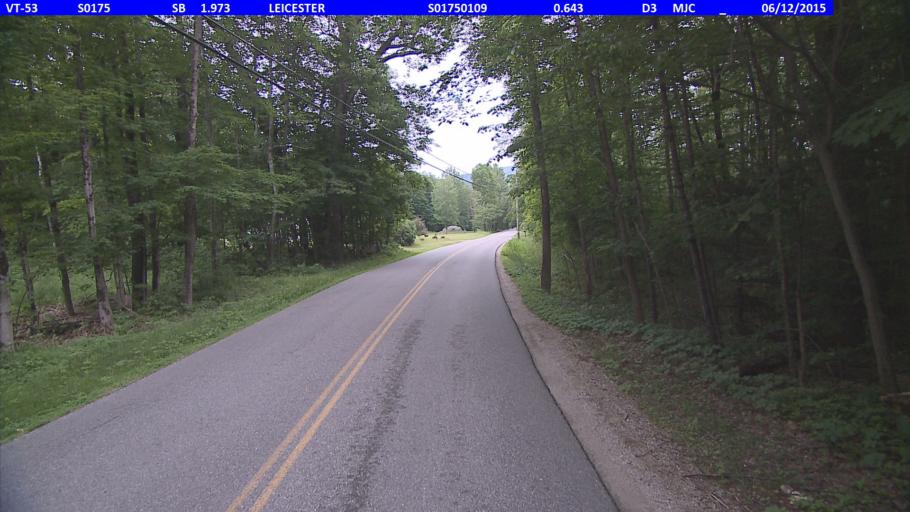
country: US
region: Vermont
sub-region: Rutland County
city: Brandon
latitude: 43.8543
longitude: -73.0628
